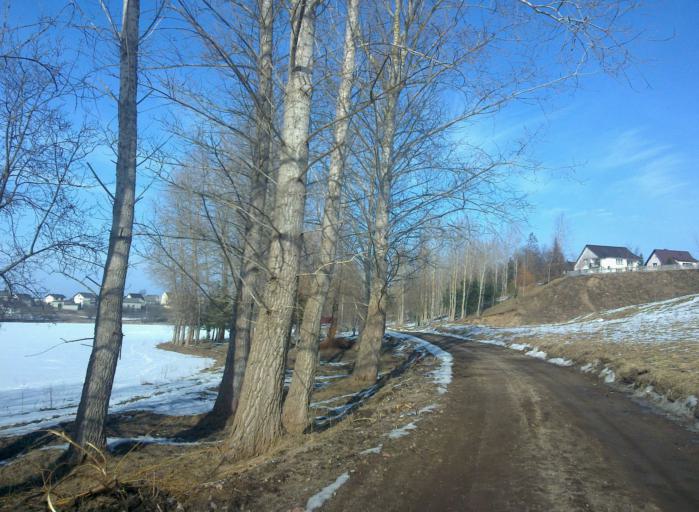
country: PL
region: Pomeranian Voivodeship
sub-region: Powiat bytowski
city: Lipnica
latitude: 53.9920
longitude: 17.4040
